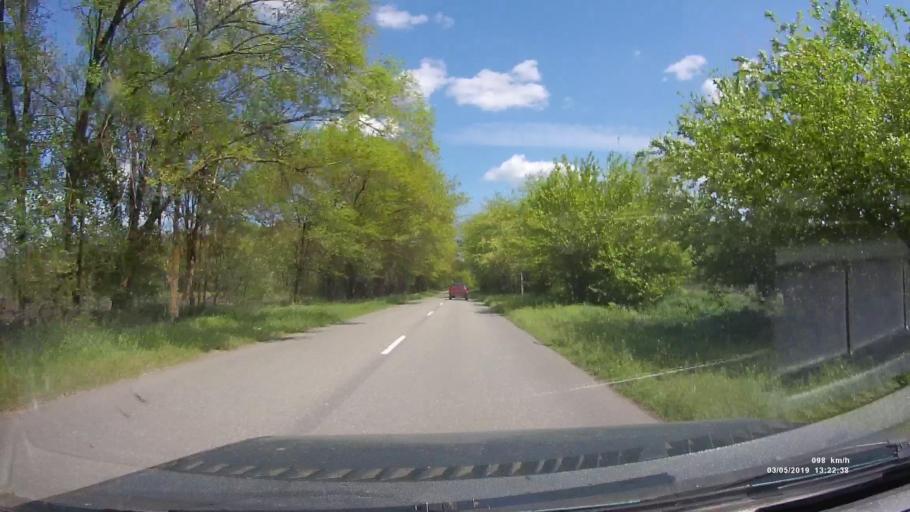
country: RU
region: Rostov
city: Semikarakorsk
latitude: 47.5622
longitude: 40.7651
